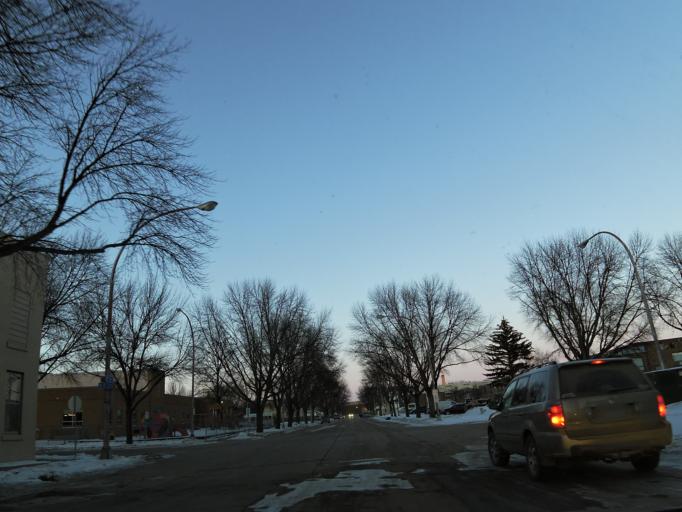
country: US
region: North Dakota
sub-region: Grand Forks County
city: Grand Forks
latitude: 47.9225
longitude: -97.0381
